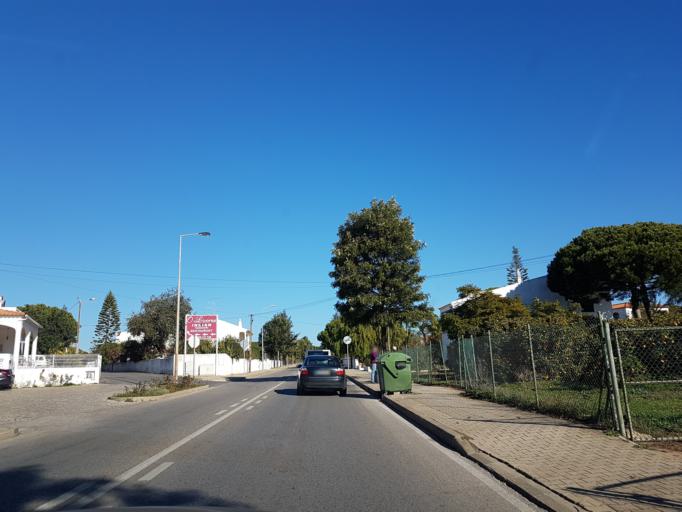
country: PT
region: Faro
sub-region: Loule
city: Boliqueime
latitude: 37.0966
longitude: -8.1868
